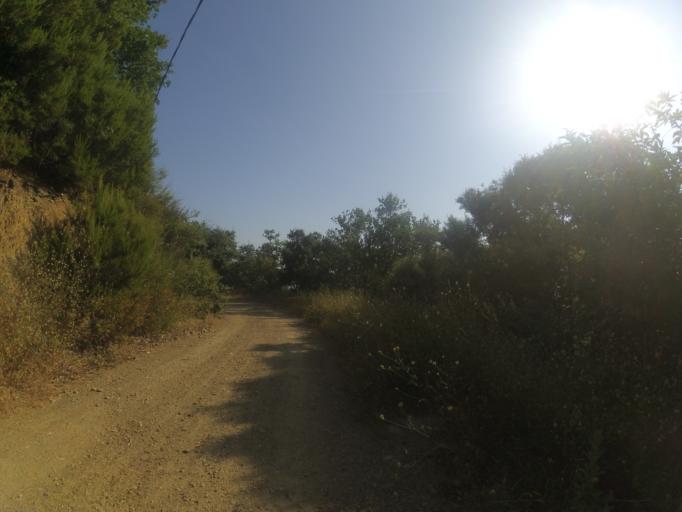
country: FR
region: Languedoc-Roussillon
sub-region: Departement des Pyrenees-Orientales
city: Ille-sur-Tet
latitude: 42.6503
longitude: 2.6487
